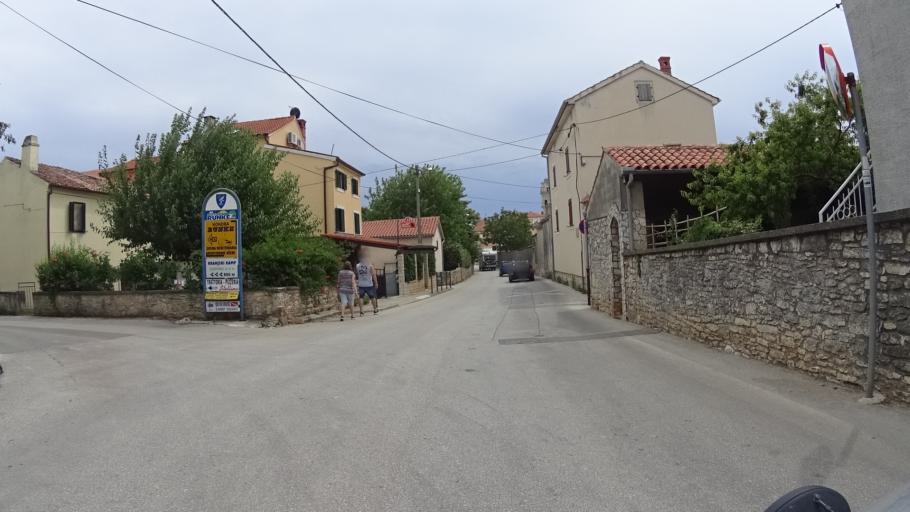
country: HR
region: Istarska
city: Medulin
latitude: 44.8035
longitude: 13.9100
